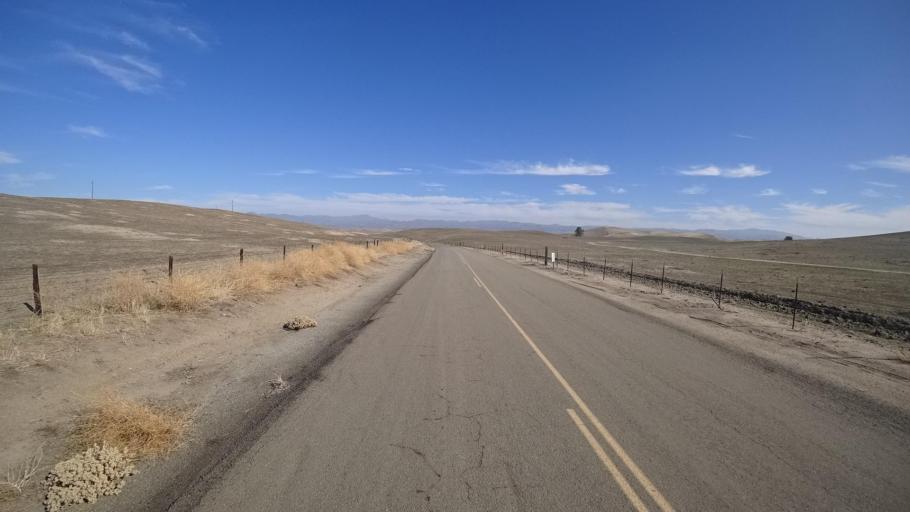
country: US
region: California
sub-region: Kern County
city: Oildale
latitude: 35.6336
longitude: -118.9535
